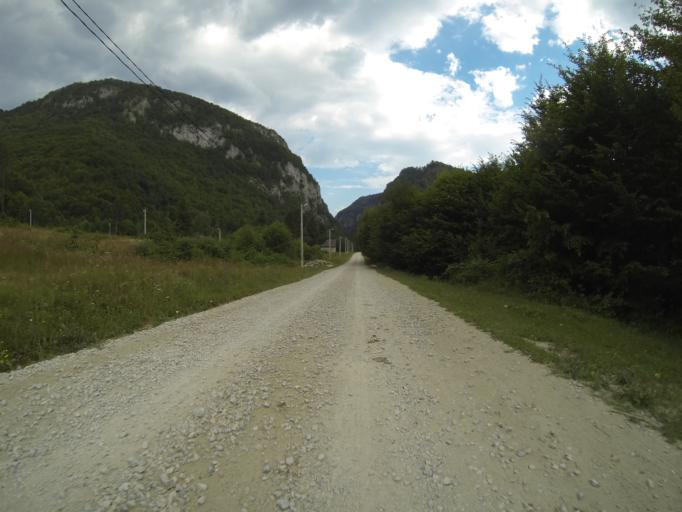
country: RO
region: Gorj
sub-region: Comuna Polovragi
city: Polovragi
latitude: 45.2164
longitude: 23.7740
